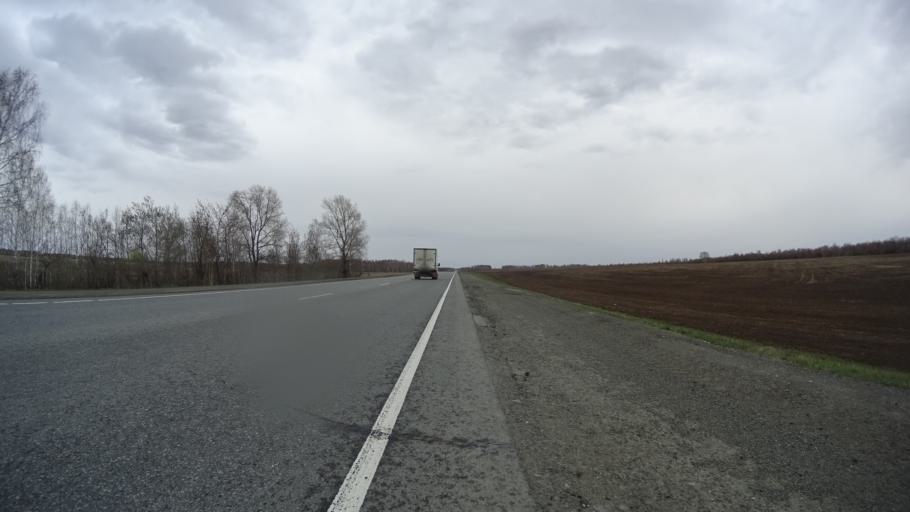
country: RU
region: Chelyabinsk
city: Krasnogorskiy
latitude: 54.6652
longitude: 61.2529
